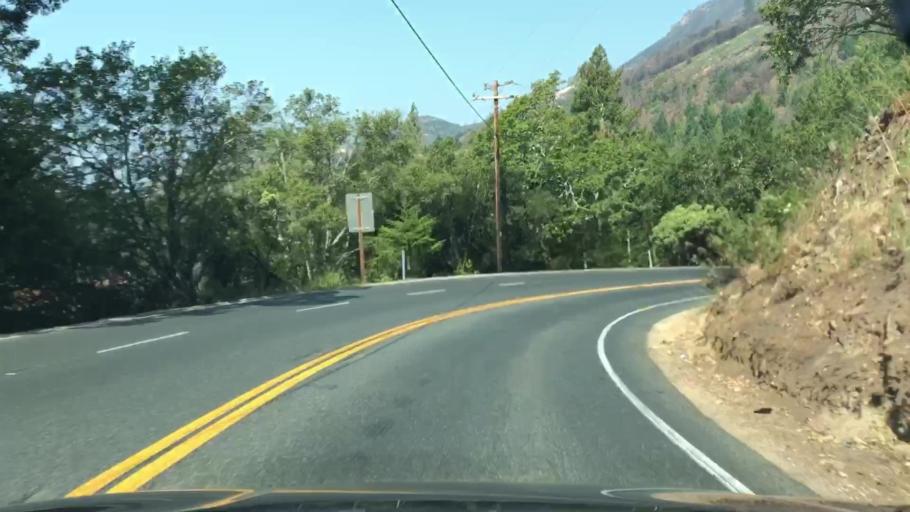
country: US
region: California
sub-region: Napa County
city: Calistoga
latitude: 38.6396
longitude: -122.5948
